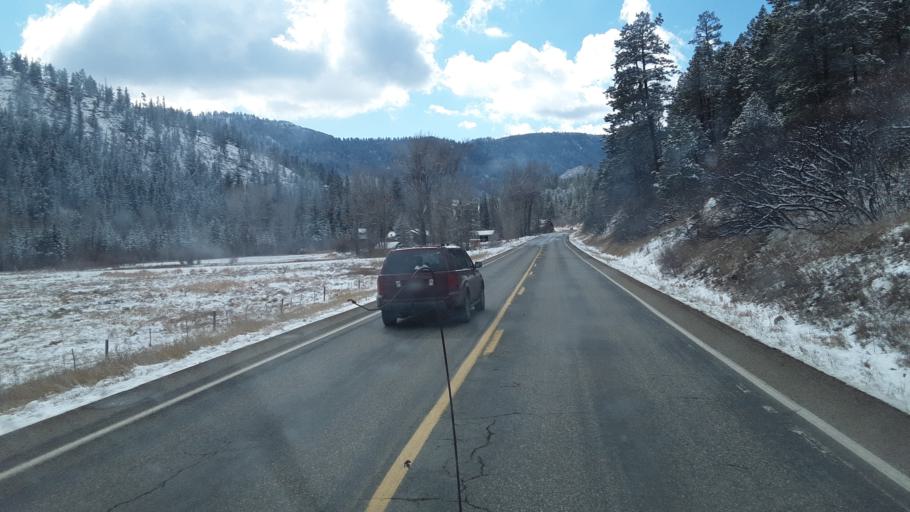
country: US
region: Colorado
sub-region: La Plata County
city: Bayfield
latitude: 37.3417
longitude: -107.7214
